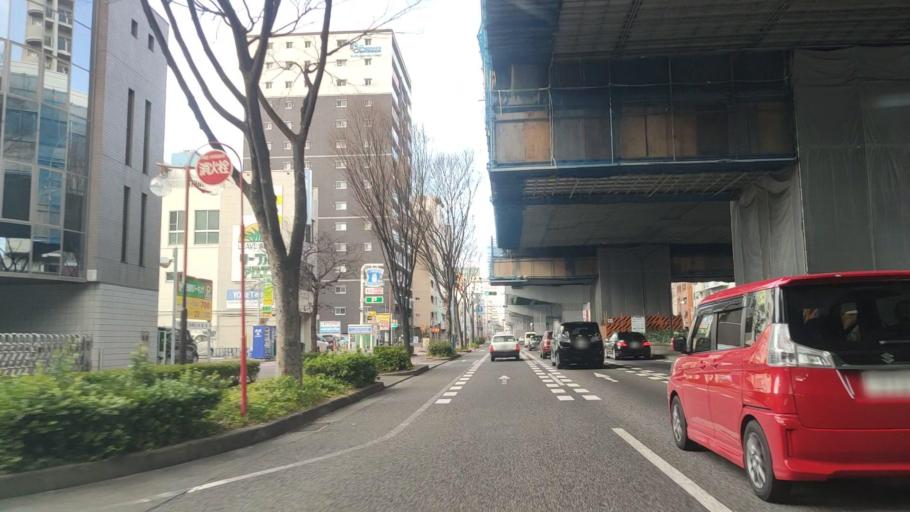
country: JP
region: Aichi
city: Nagoya-shi
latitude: 35.1634
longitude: 136.9151
